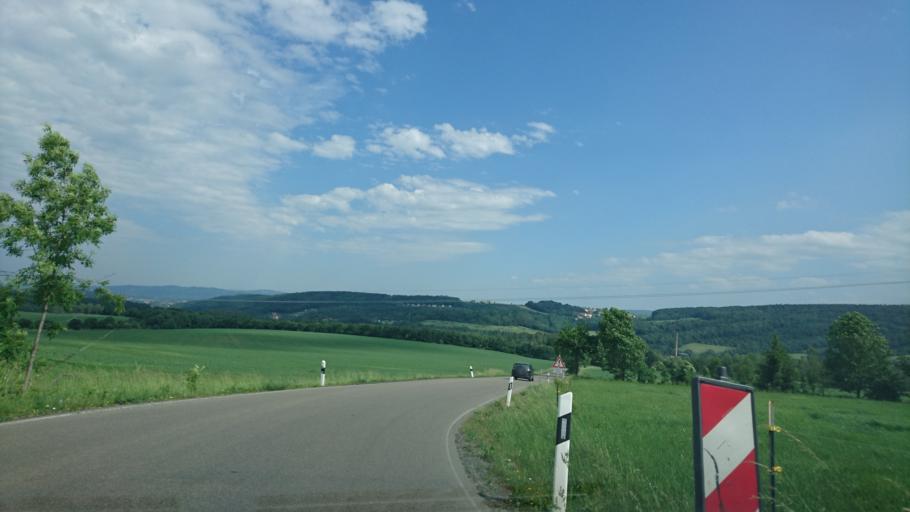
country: DE
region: Saxony
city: Dohma
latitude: 50.9065
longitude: 13.9695
